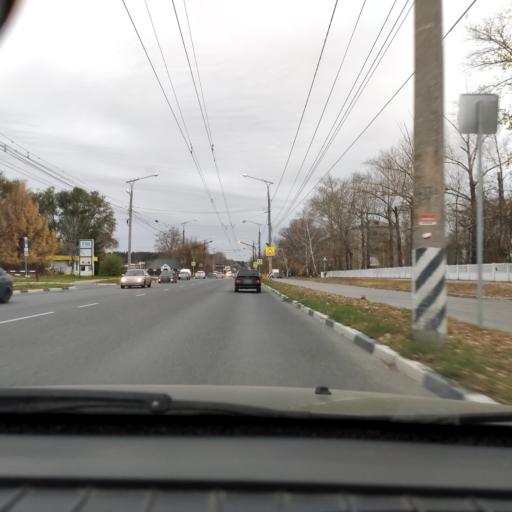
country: RU
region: Samara
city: Tol'yatti
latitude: 53.5007
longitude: 49.4192
